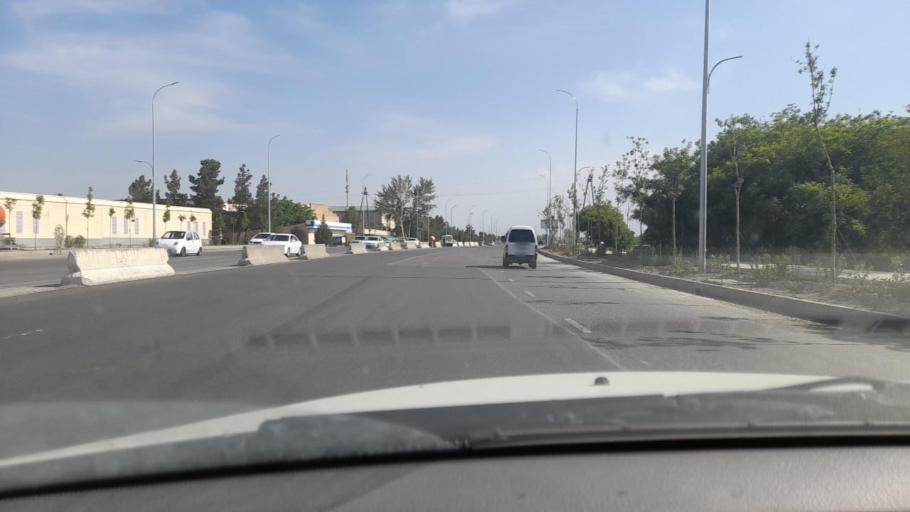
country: UZ
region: Samarqand
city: Daxbet
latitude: 39.7576
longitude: 66.9191
